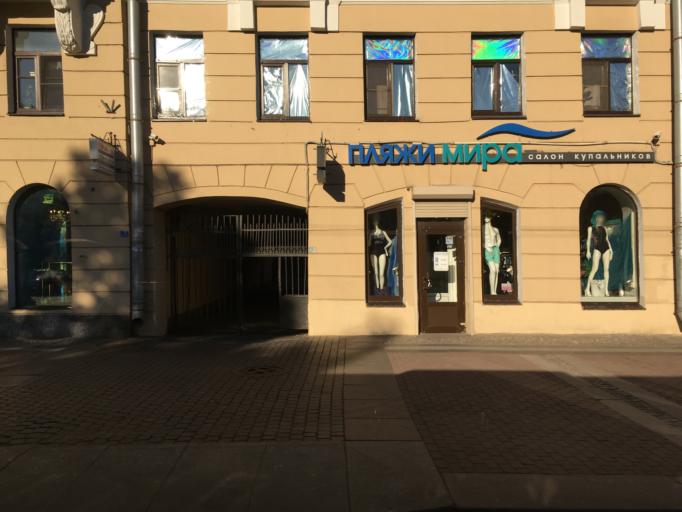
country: RU
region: St.-Petersburg
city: Admiralteisky
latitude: 59.8871
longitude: 30.3202
